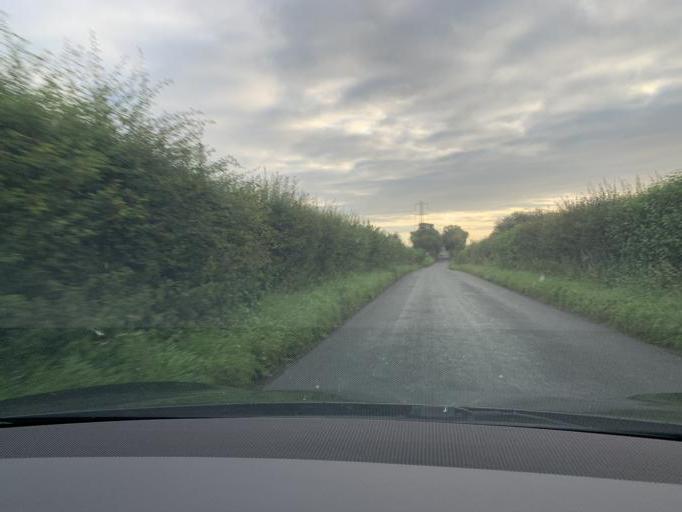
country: GB
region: England
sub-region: Wiltshire
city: Great Bedwyn
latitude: 51.3384
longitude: -1.6073
